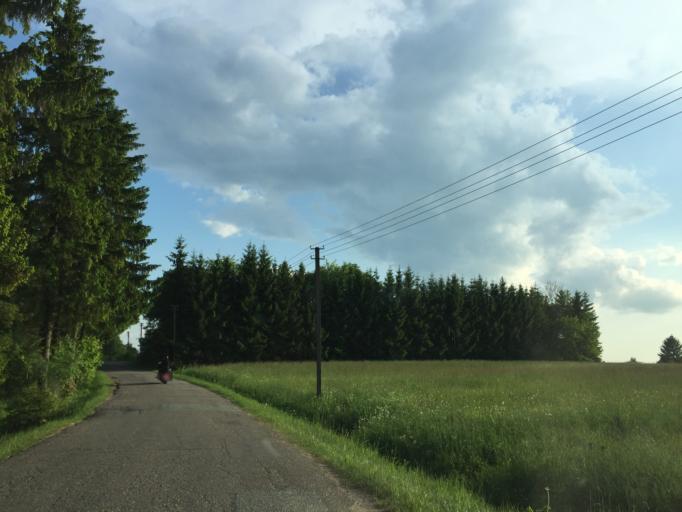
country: LT
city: Plateliai
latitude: 56.0492
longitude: 21.8254
